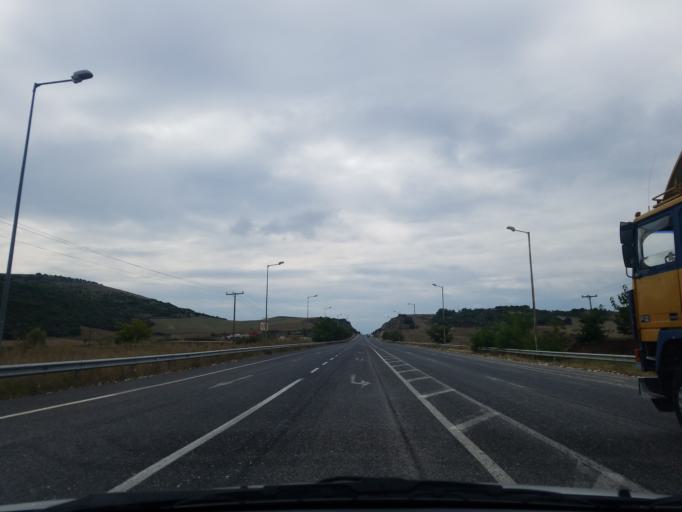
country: GR
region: Central Greece
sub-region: Nomos Fthiotidos
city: Domokos
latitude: 39.1111
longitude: 22.3079
